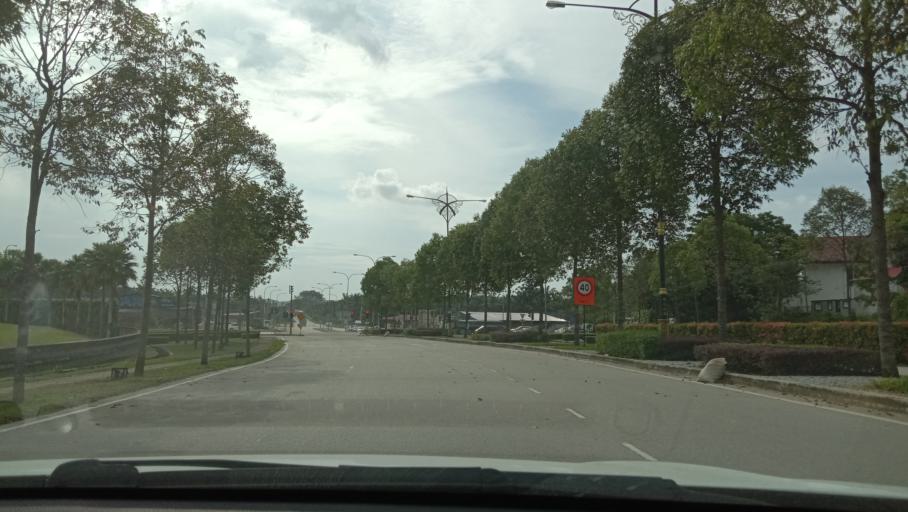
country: MY
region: Selangor
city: Ladang Seri Kundang
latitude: 3.2473
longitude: 101.4734
